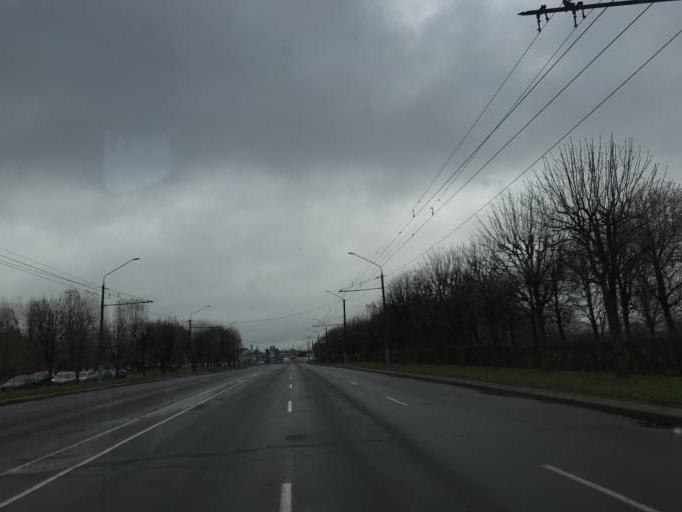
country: BY
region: Mogilev
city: Mahilyow
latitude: 53.8641
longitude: 30.3334
